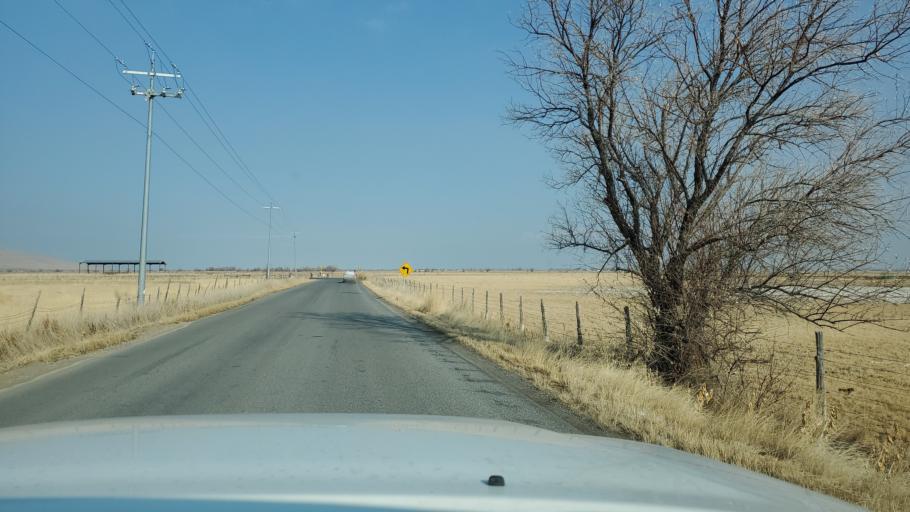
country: US
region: Utah
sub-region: Utah County
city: West Mountain
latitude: 40.0983
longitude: -111.7883
